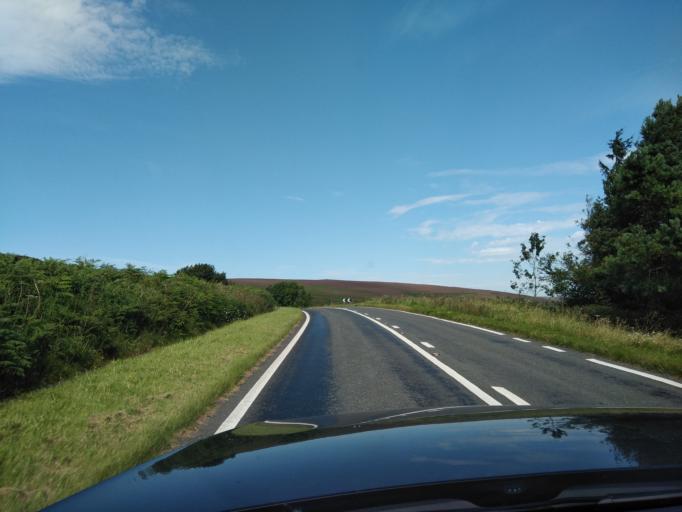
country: GB
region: England
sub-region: Derbyshire
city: Dronfield
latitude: 53.2984
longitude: -1.5547
